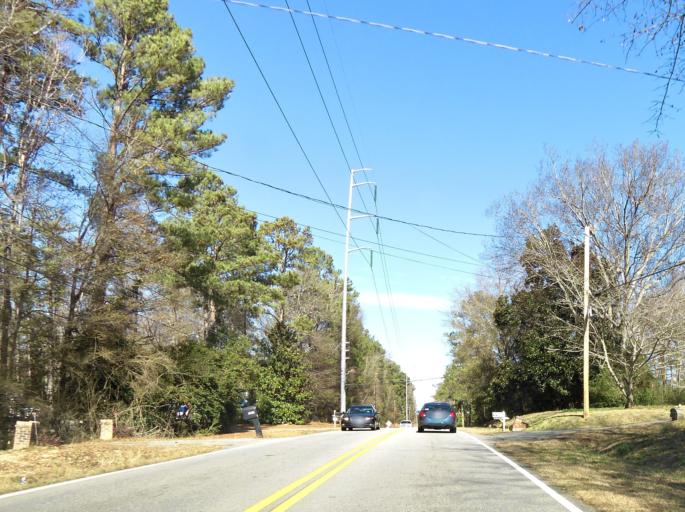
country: US
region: Georgia
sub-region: Bibb County
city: West Point
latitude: 32.8516
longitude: -83.7465
